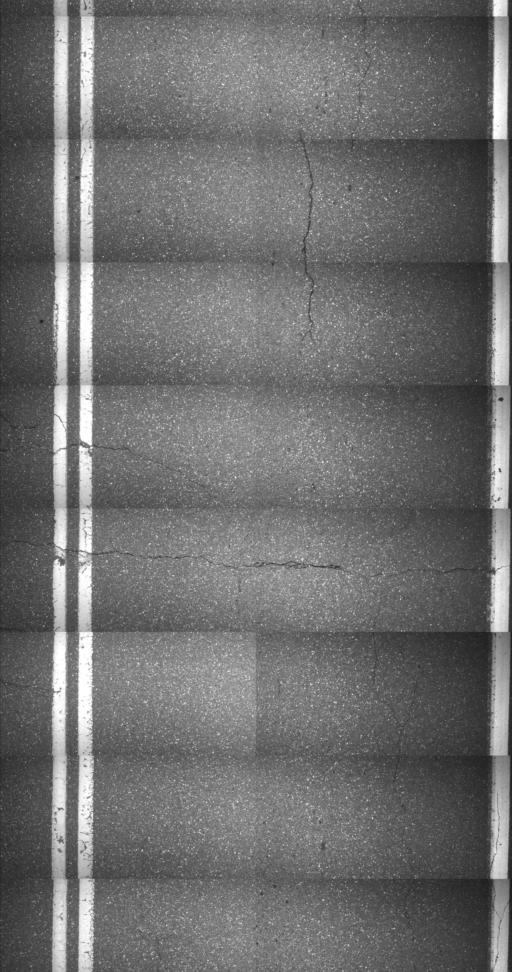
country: US
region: Vermont
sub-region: Windsor County
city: Woodstock
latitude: 43.5828
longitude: -72.6575
